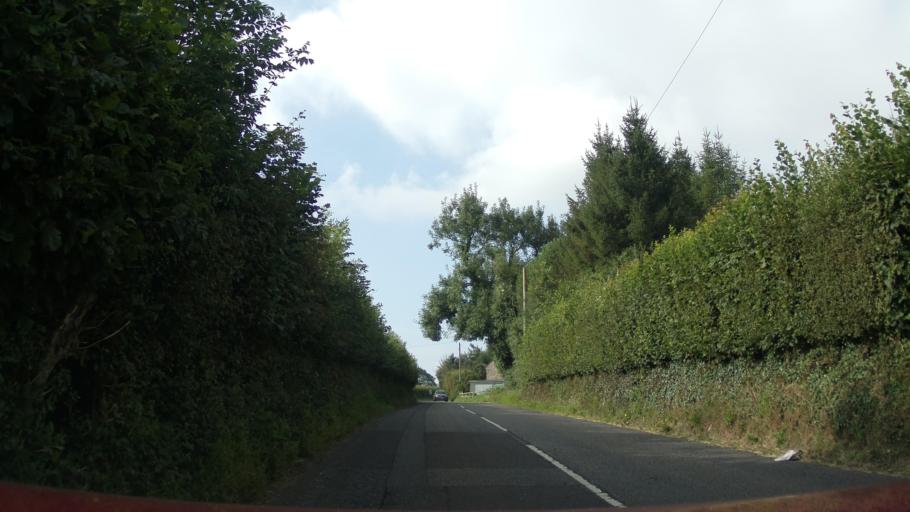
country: GB
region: England
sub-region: Bath and North East Somerset
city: Chew Magna
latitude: 51.3656
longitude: -2.6319
